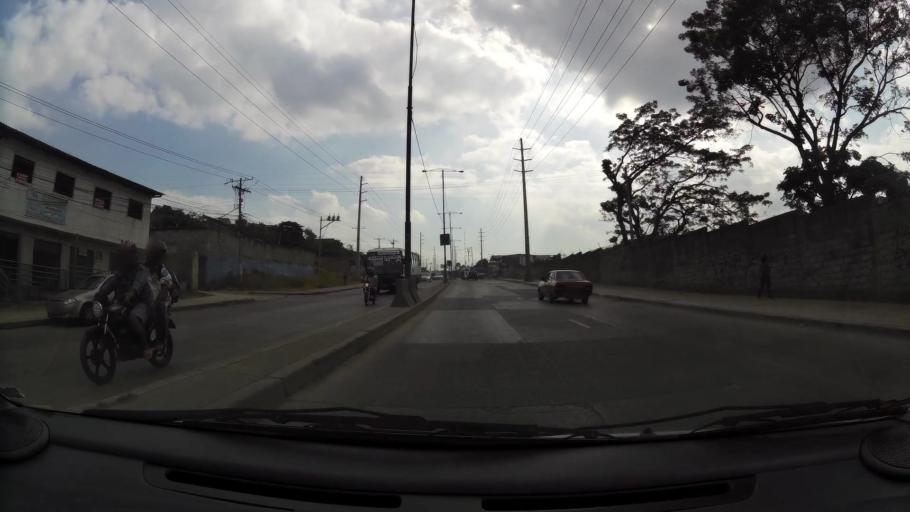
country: EC
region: Guayas
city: Santa Lucia
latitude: -2.1185
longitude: -79.9618
